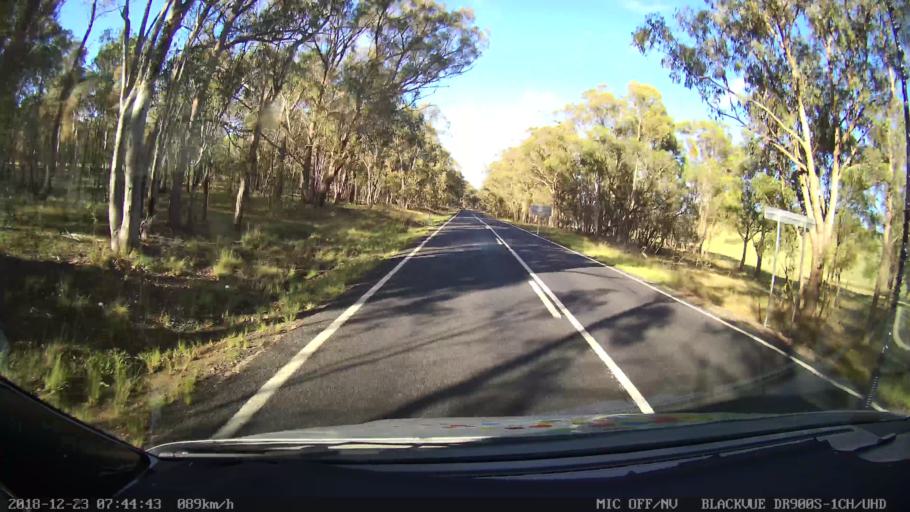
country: AU
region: New South Wales
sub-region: Armidale Dumaresq
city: Enmore
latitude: -30.5247
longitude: 151.9461
